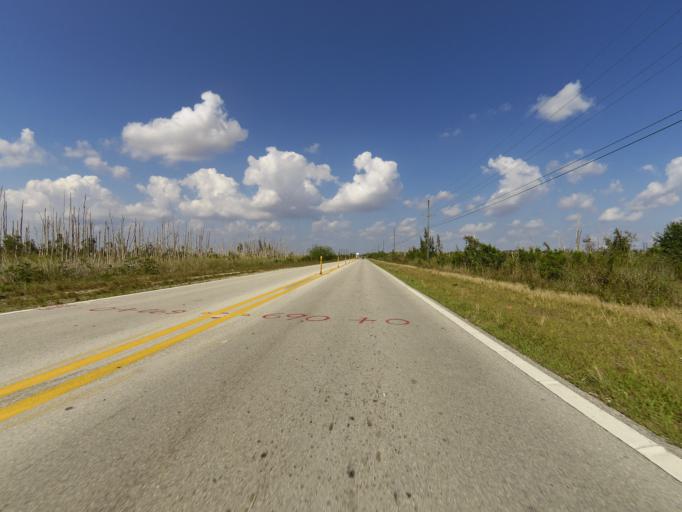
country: US
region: Florida
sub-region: Miami-Dade County
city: Palm Springs North
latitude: 25.9331
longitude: -80.4472
